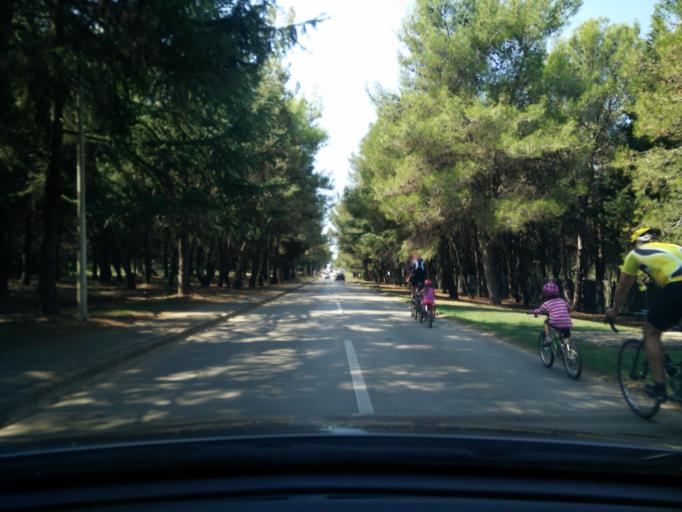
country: HR
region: Istarska
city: Novigrad
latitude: 45.2952
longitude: 13.5879
